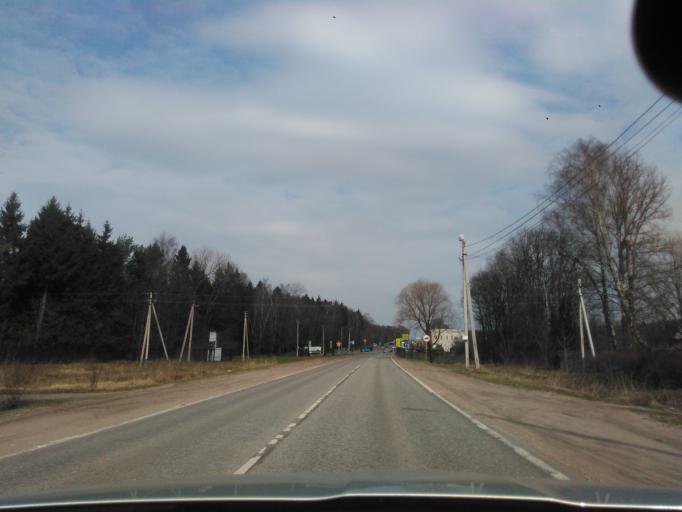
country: RU
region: Moskovskaya
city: Marfino
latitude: 56.0531
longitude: 37.5312
